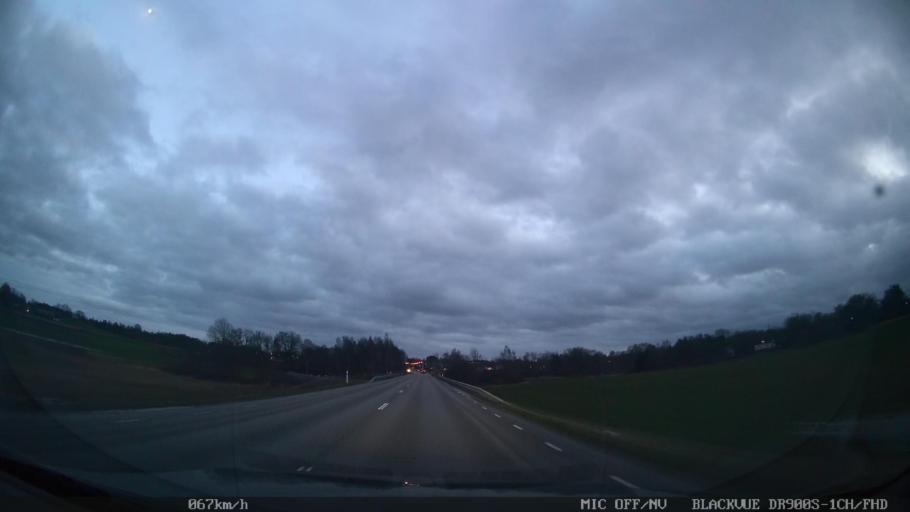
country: SE
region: Skane
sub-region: Hassleholms Kommun
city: Hassleholm
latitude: 56.1753
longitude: 13.7560
